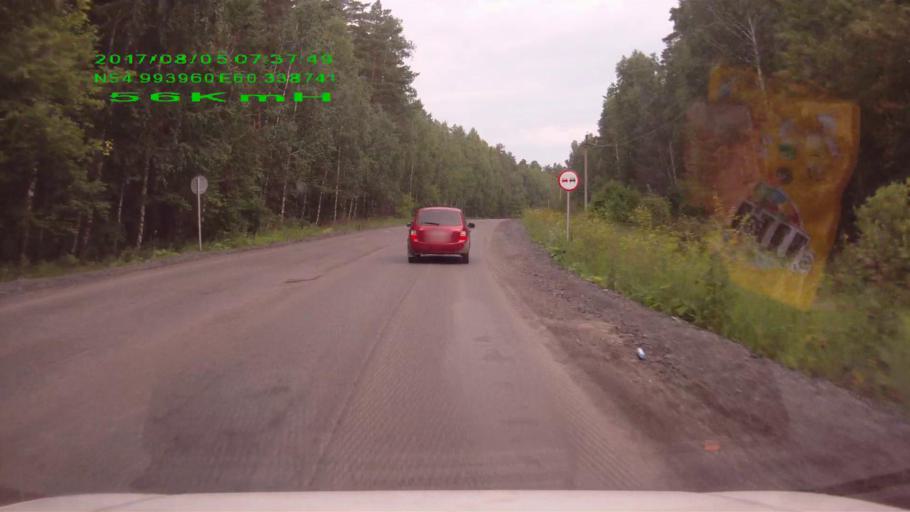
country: RU
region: Chelyabinsk
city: Chebarkul'
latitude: 54.9941
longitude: 60.3386
